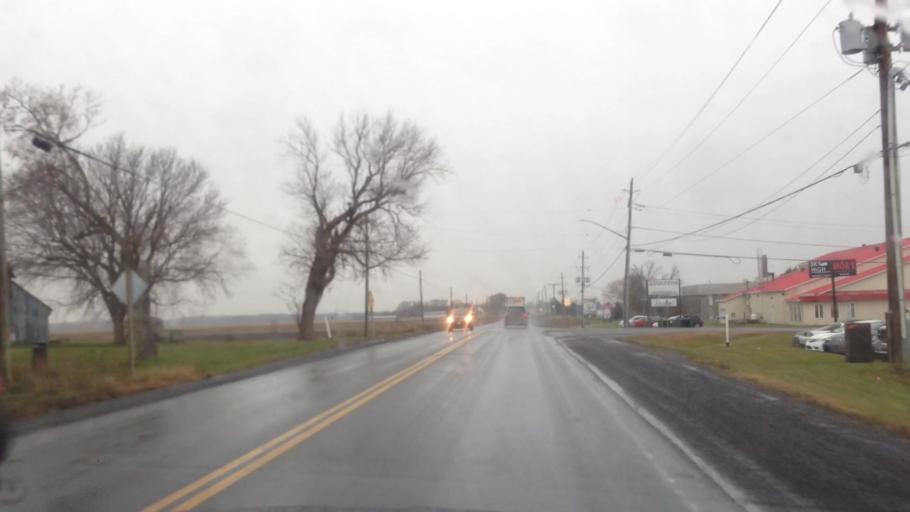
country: CA
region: Ontario
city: Bourget
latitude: 45.3300
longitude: -75.3453
